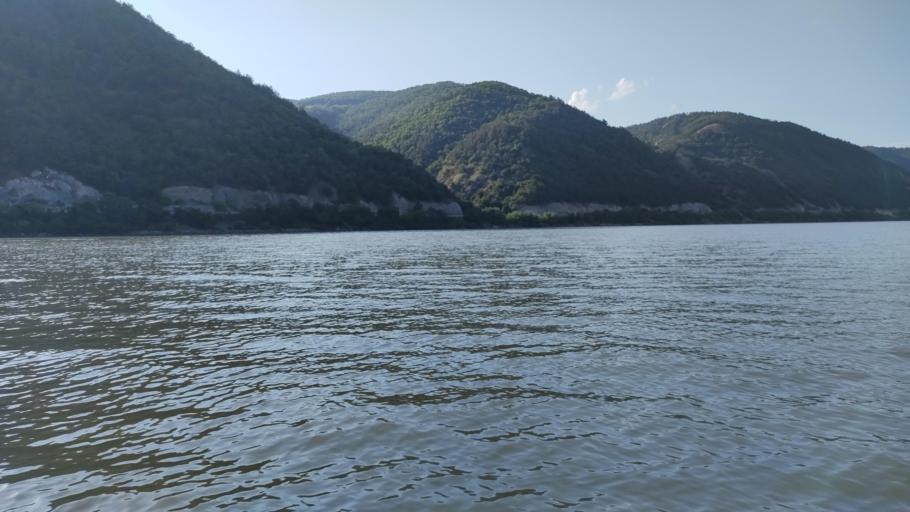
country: RO
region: Mehedinti
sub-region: Comuna Svinita
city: Svinita
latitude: 44.4976
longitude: 22.1900
